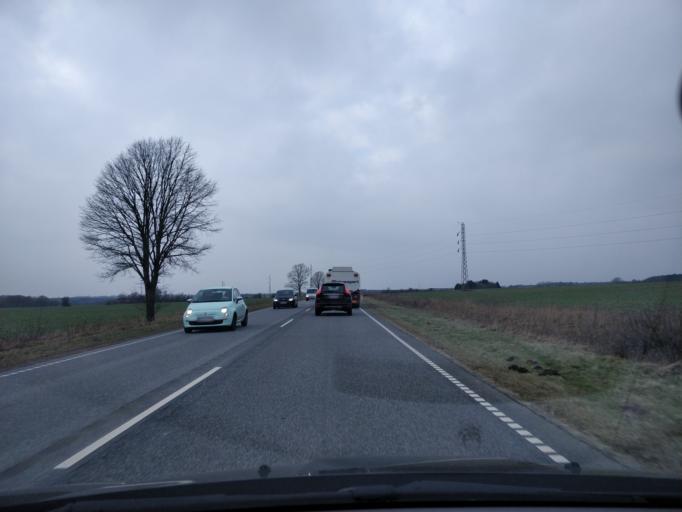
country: DK
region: South Denmark
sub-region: Vejle Kommune
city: Borkop
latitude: 55.6615
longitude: 9.6142
